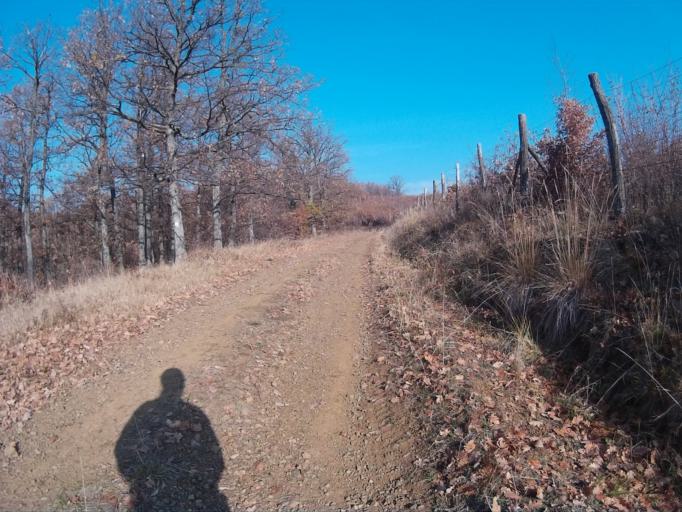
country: HU
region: Heves
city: Belapatfalva
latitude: 48.0207
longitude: 20.3953
